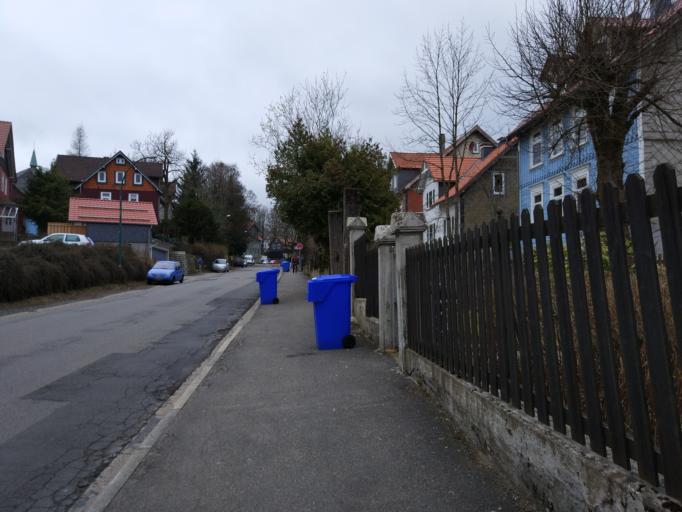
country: DE
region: Lower Saxony
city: Clausthal-Zellerfeld
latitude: 51.8052
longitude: 10.3408
